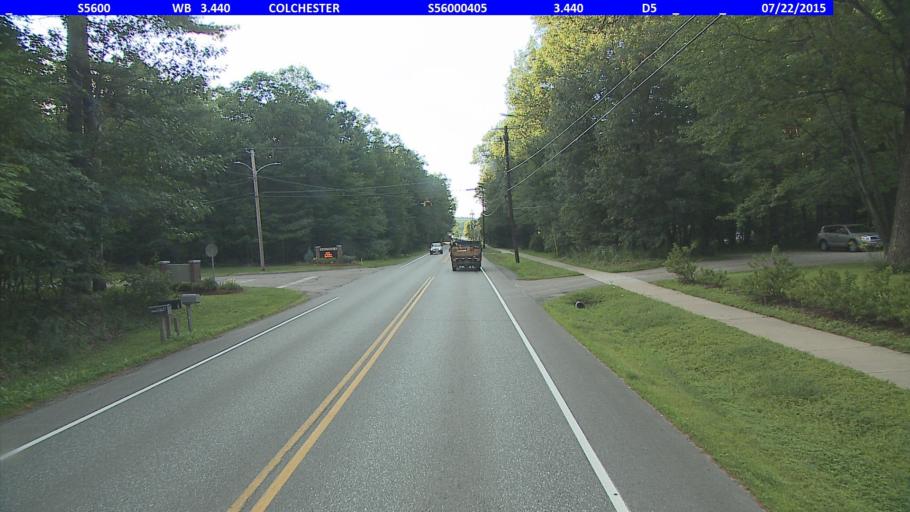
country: US
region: Vermont
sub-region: Chittenden County
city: Winooski
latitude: 44.5419
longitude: -73.2127
